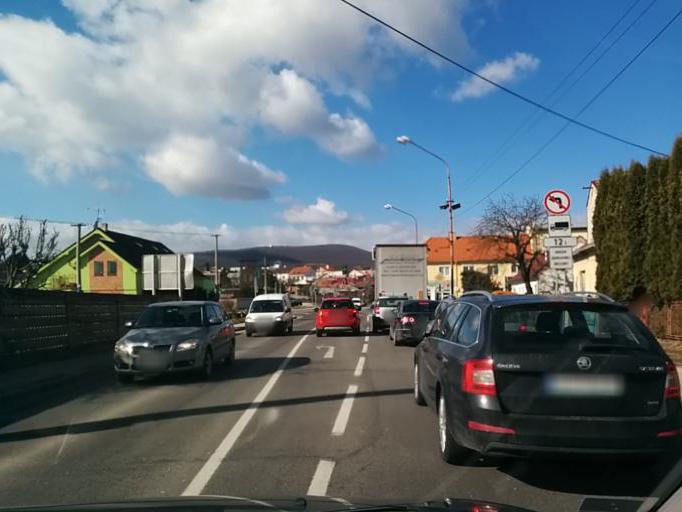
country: SK
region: Trenciansky
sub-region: Okres Nove Mesto nad Vahom
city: Nove Mesto nad Vahom
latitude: 48.7650
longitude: 17.8356
